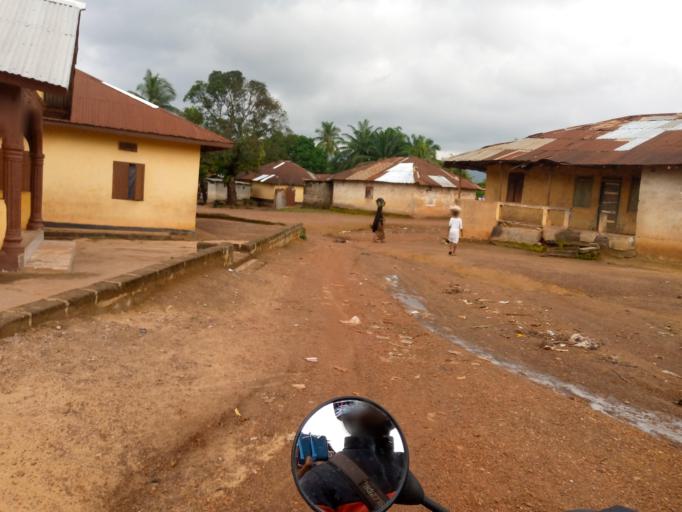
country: SL
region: Eastern Province
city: Kenema
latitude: 7.8642
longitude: -11.1889
